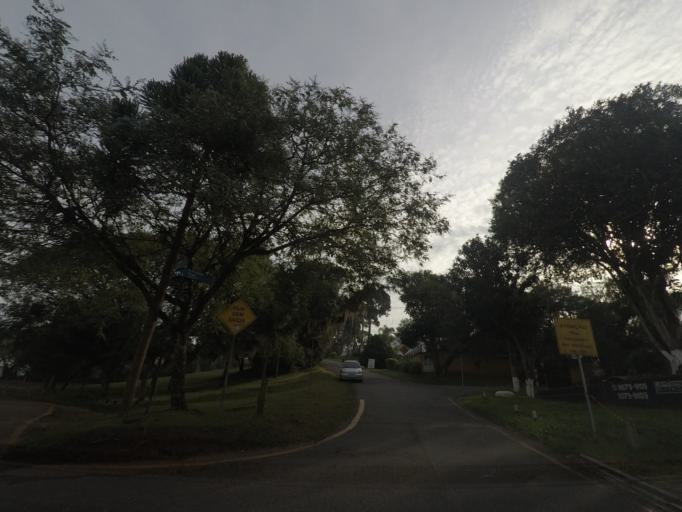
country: BR
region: Parana
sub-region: Curitiba
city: Curitiba
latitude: -25.4215
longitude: -49.3052
